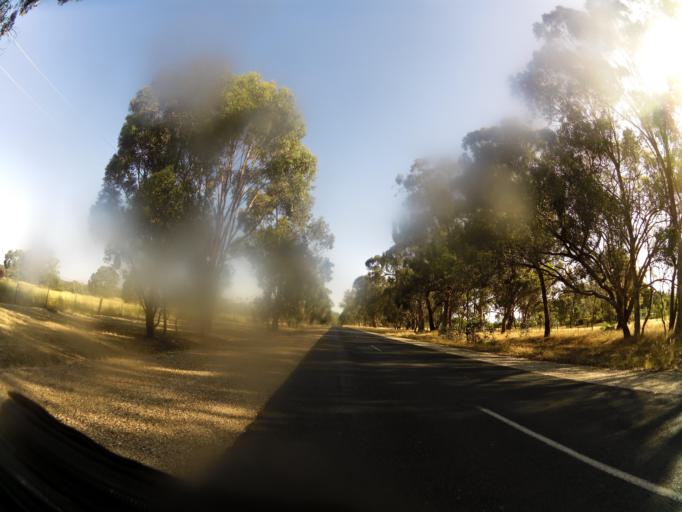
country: AU
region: Victoria
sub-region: Murrindindi
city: Kinglake West
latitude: -36.9940
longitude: 145.1128
